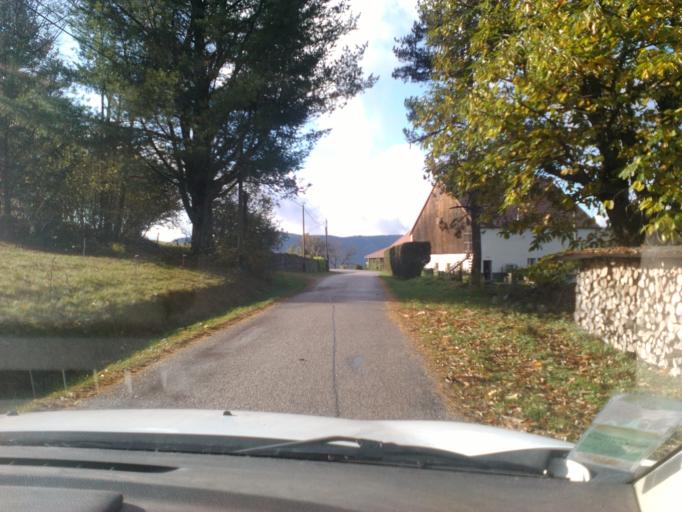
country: FR
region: Lorraine
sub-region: Departement des Vosges
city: Saulxures-sur-Moselotte
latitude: 47.9691
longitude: 6.7921
